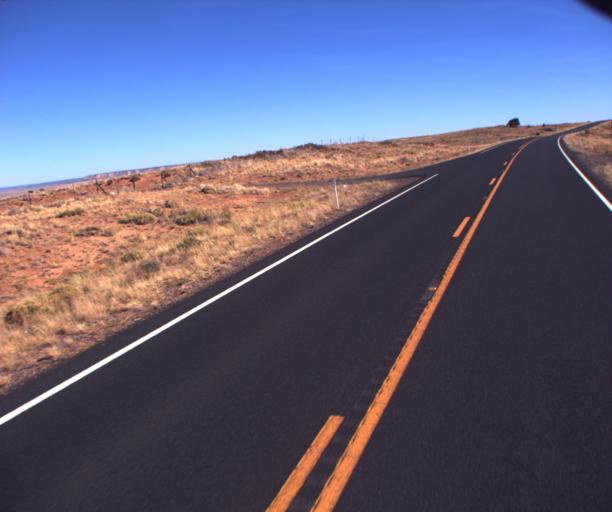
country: US
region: Arizona
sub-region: Apache County
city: Ganado
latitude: 35.7872
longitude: -109.6735
